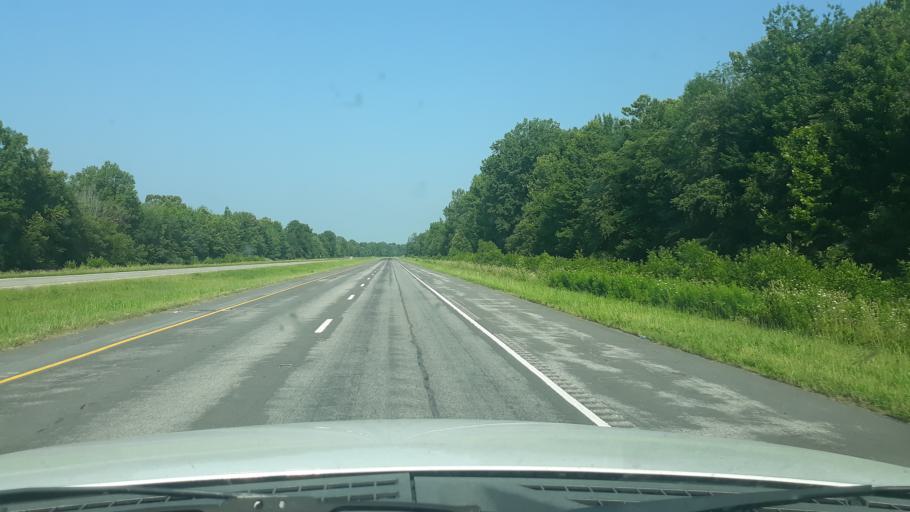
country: US
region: Illinois
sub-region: Saline County
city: Carrier Mills
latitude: 37.7343
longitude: -88.6854
